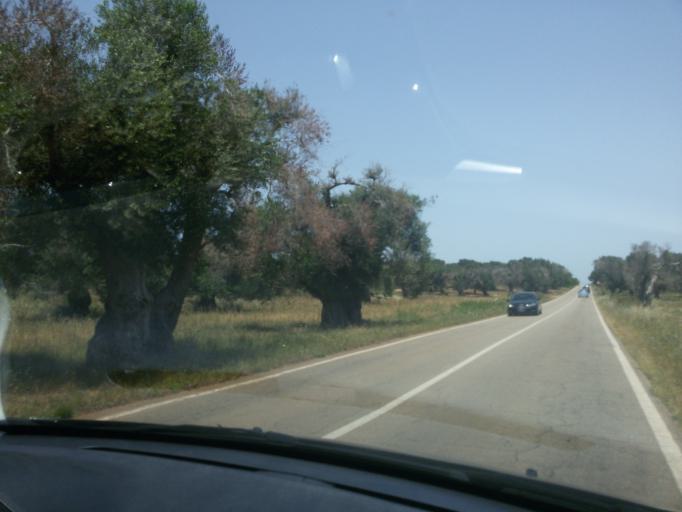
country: IT
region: Apulia
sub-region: Provincia di Lecce
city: Porto Cesareo
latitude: 40.2937
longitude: 17.9156
